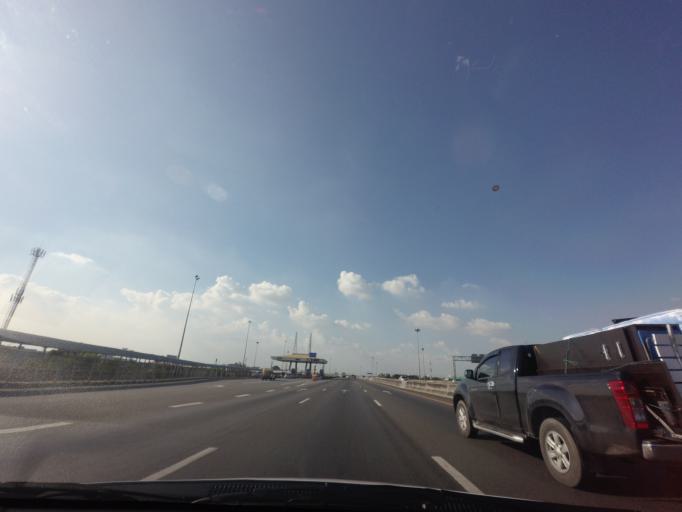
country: TH
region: Samut Prakan
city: Samut Prakan
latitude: 13.6085
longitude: 100.6245
